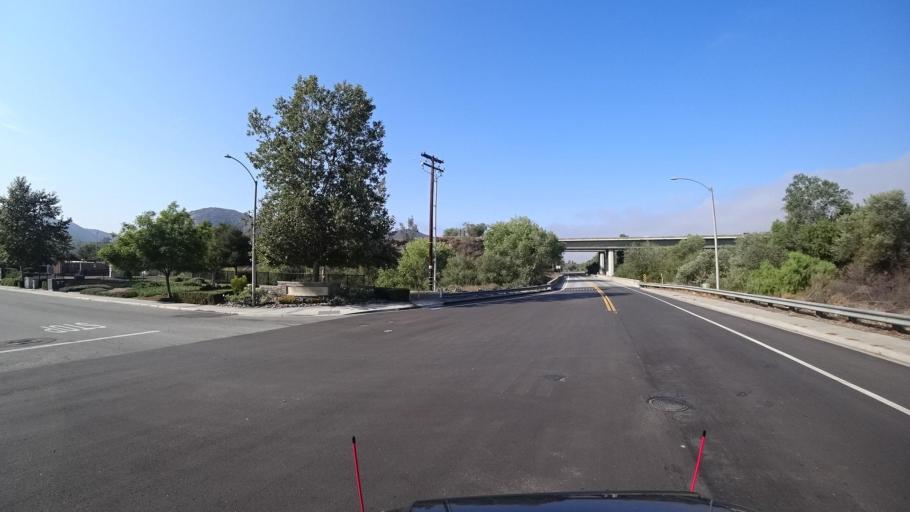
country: US
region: California
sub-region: San Diego County
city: Bonsall
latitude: 33.3244
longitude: -117.1567
